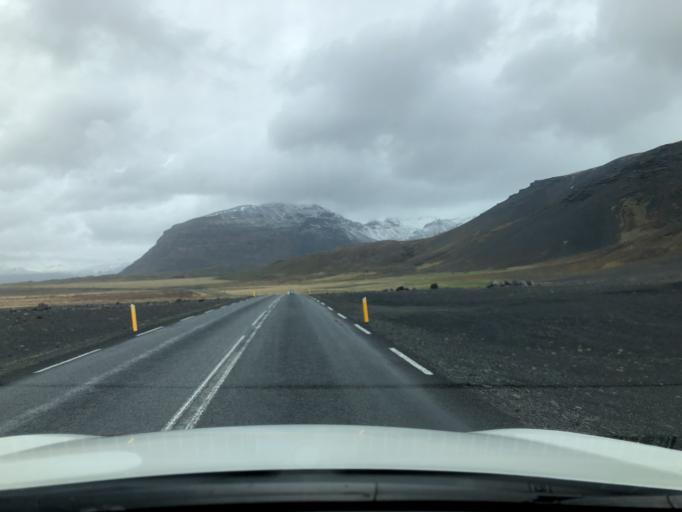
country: IS
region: East
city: Hoefn
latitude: 63.9350
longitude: -16.7934
